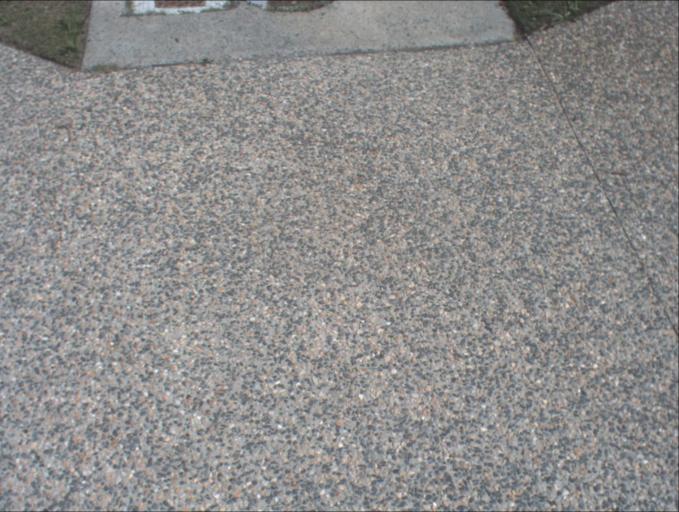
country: AU
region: Queensland
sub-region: Logan
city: Waterford West
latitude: -27.7179
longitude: 153.1551
